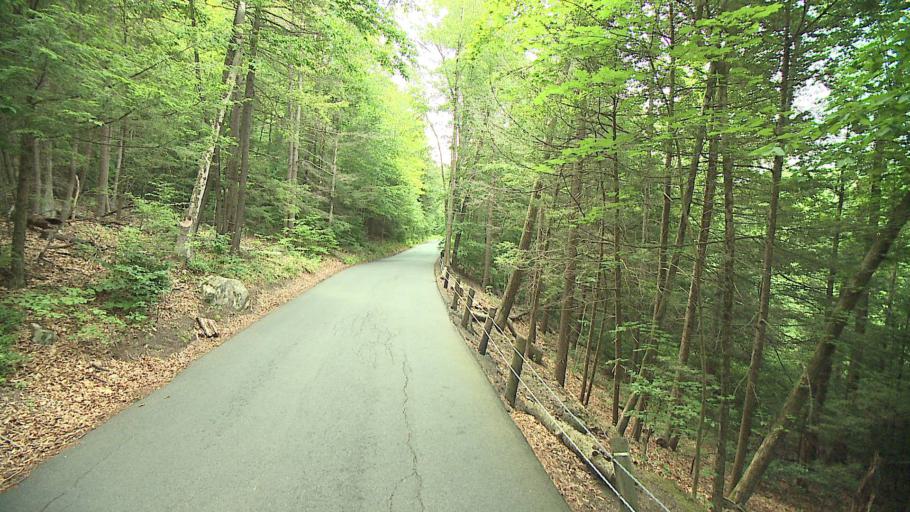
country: US
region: Connecticut
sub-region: Litchfield County
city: Winsted
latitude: 41.9418
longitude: -73.0064
